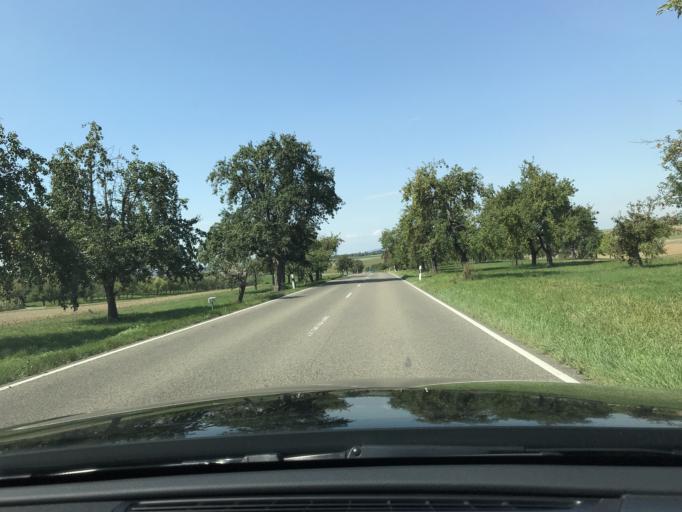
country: DE
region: Baden-Wuerttemberg
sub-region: Regierungsbezirk Stuttgart
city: Erdmannhausen
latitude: 48.9267
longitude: 9.3093
